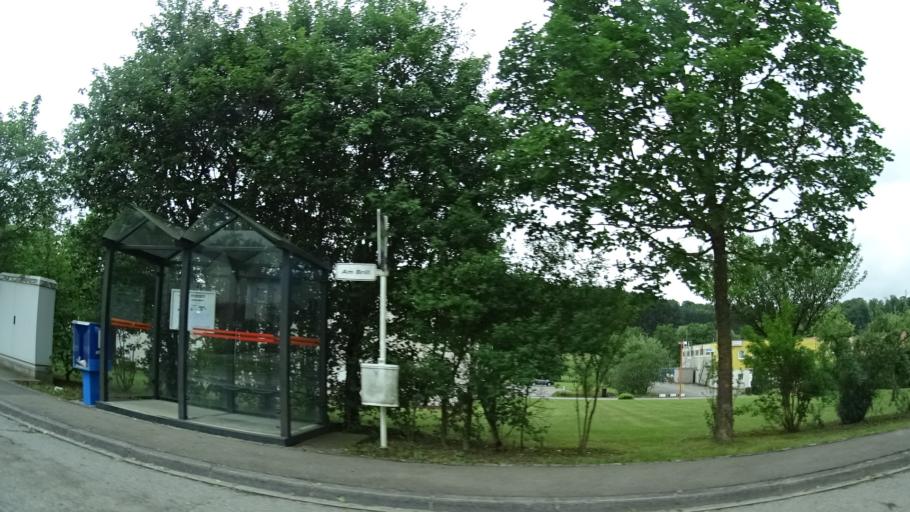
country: LU
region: Luxembourg
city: Pontpierre
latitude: 49.5461
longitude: 6.0151
